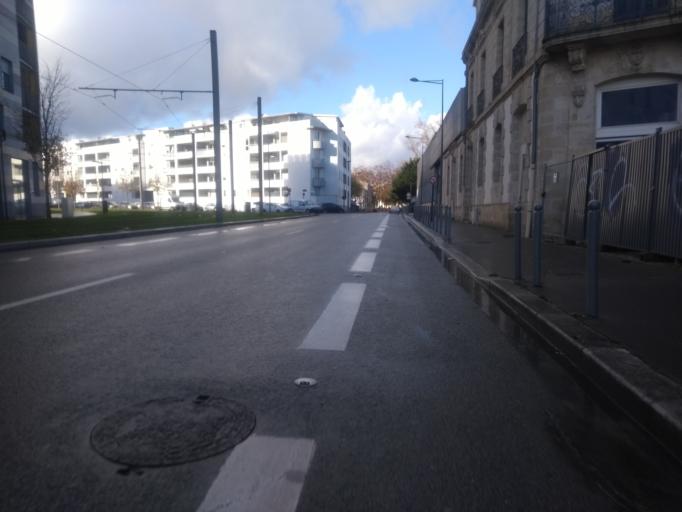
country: FR
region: Aquitaine
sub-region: Departement de la Gironde
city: Begles
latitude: 44.8219
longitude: -0.5504
